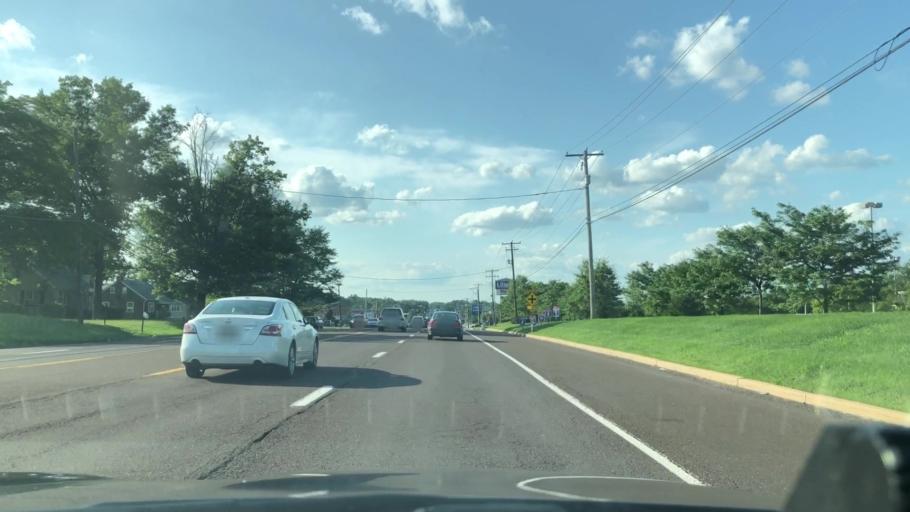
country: US
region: Pennsylvania
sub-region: Bucks County
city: Quakertown
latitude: 40.4193
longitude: -75.3449
